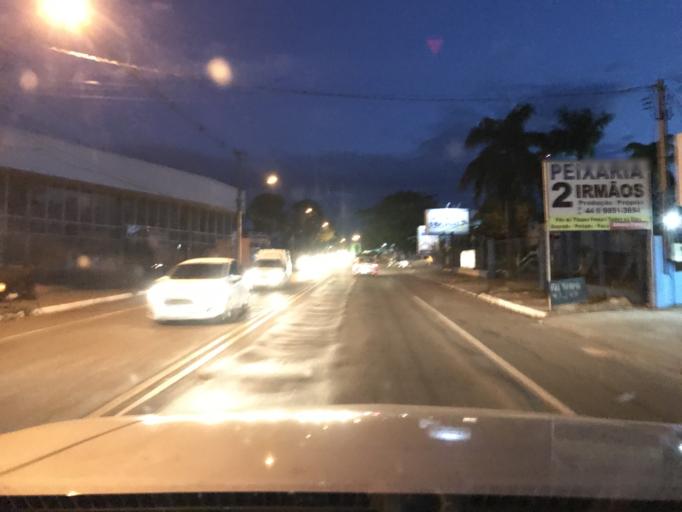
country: PY
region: Canindeyu
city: Salto del Guaira
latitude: -24.0807
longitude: -54.2436
